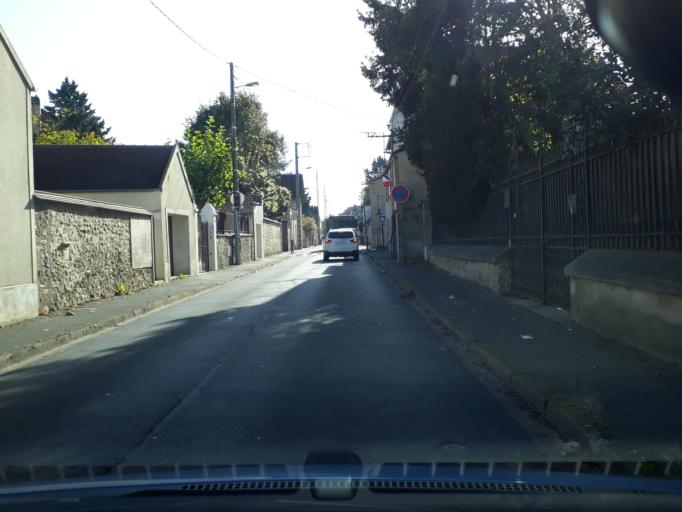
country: FR
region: Ile-de-France
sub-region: Departement de Seine-et-Marne
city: Chartrettes
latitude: 48.4911
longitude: 2.6966
